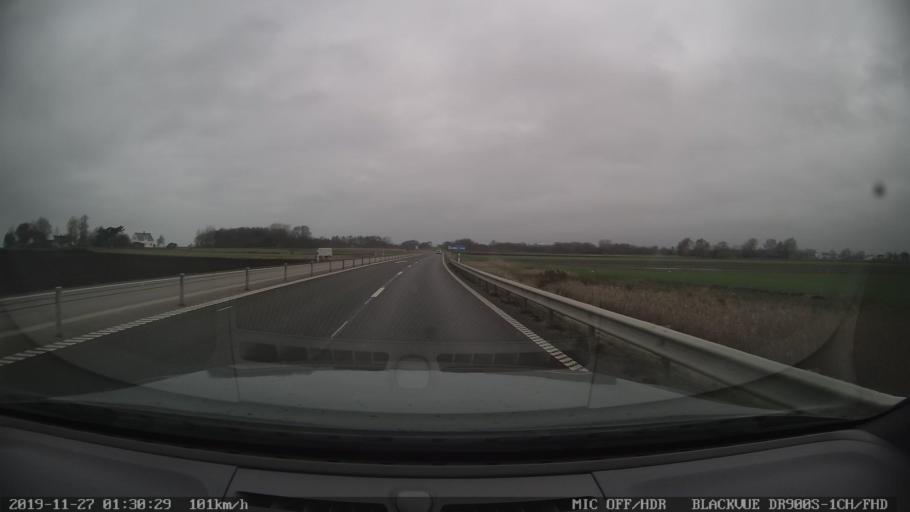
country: SE
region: Skane
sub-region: Hoganas Kommun
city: Hoganas
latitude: 56.1684
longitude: 12.5689
